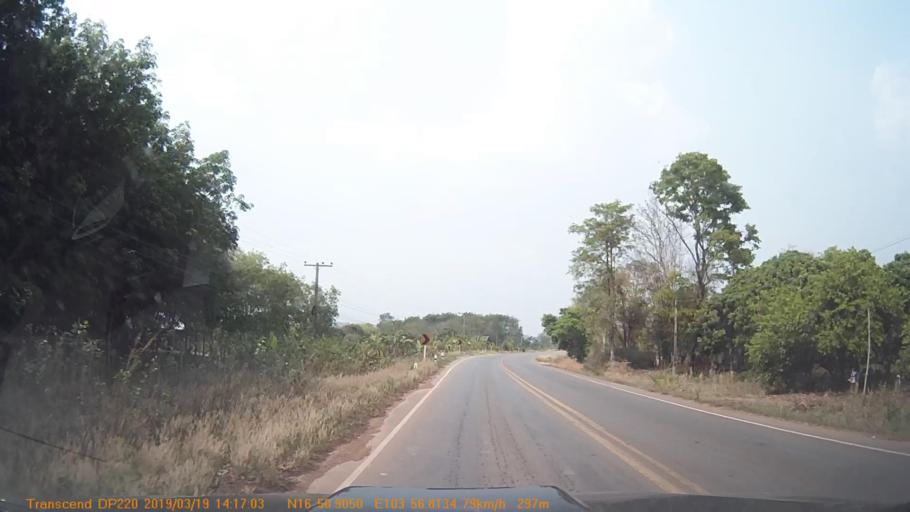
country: TH
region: Kalasin
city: Na Khu
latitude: 16.8490
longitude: 103.9469
